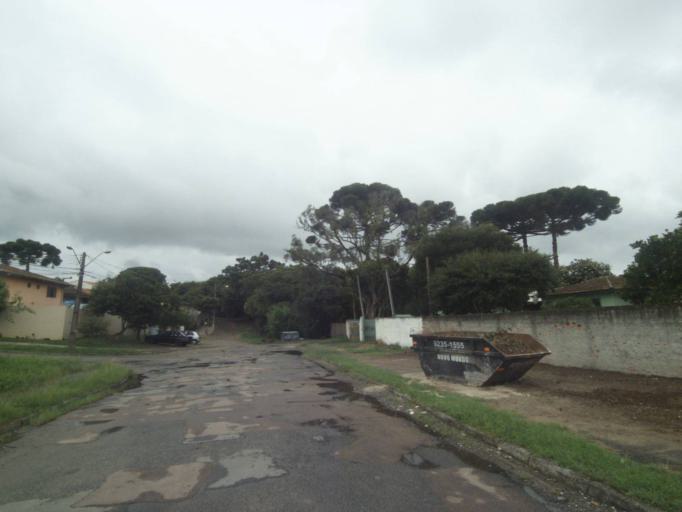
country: BR
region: Parana
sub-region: Curitiba
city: Curitiba
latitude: -25.4864
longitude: -49.2829
